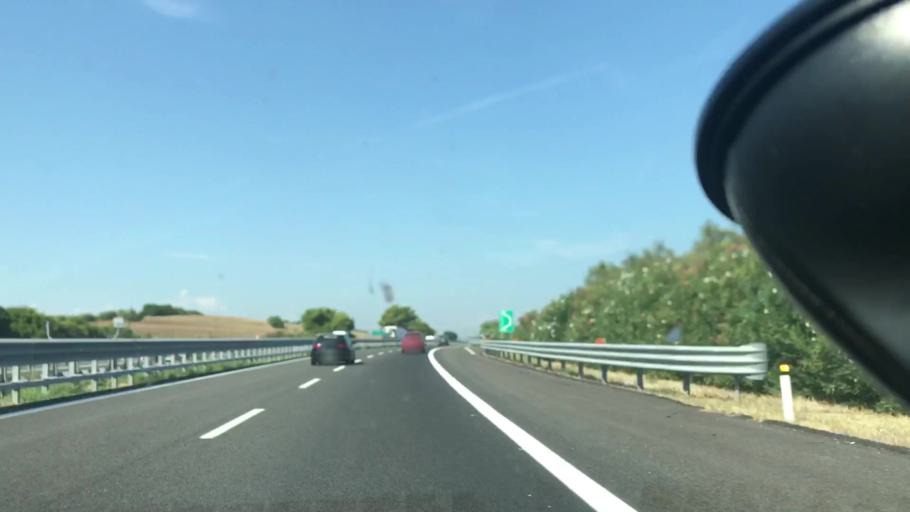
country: IT
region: Molise
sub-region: Provincia di Campobasso
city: Petacciato
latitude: 42.0201
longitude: 14.8927
